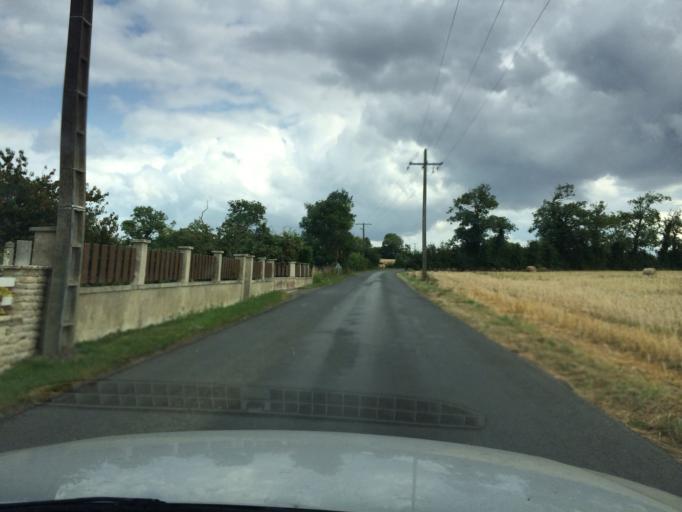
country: FR
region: Lower Normandy
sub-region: Departement du Calvados
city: Saint-Vigor-le-Grand
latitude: 49.3002
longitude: -0.6906
